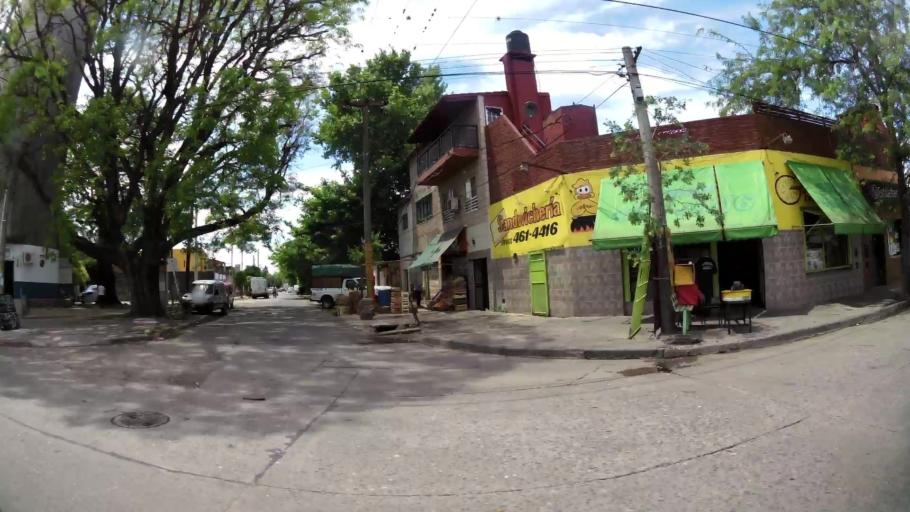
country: AR
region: Santa Fe
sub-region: Departamento de Rosario
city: Rosario
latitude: -32.9868
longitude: -60.6282
